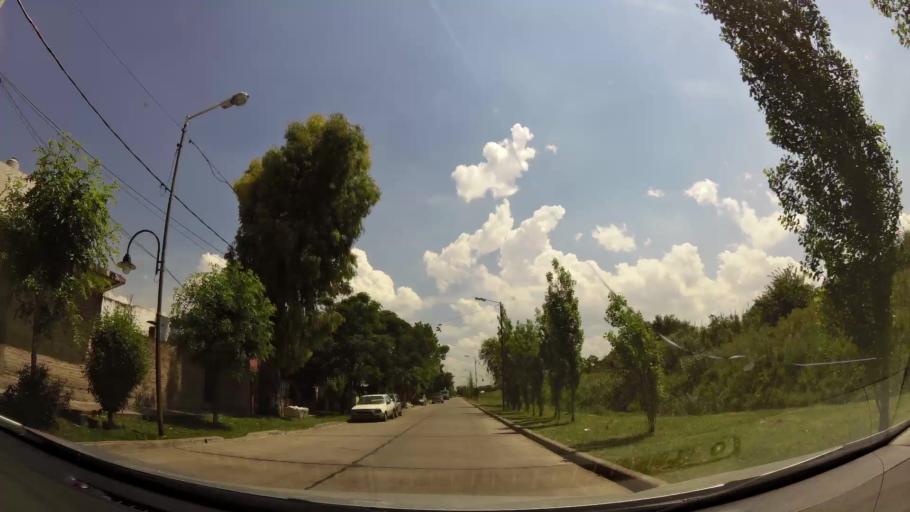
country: AR
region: Buenos Aires
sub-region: Partido de Tigre
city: Tigre
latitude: -34.4655
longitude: -58.5869
